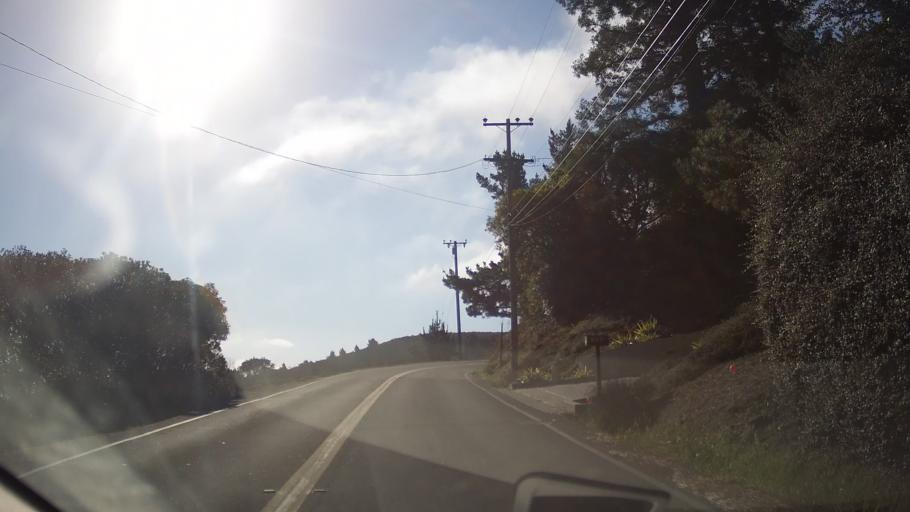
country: US
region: California
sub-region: Marin County
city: Mill Valley
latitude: 37.8953
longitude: -122.5574
